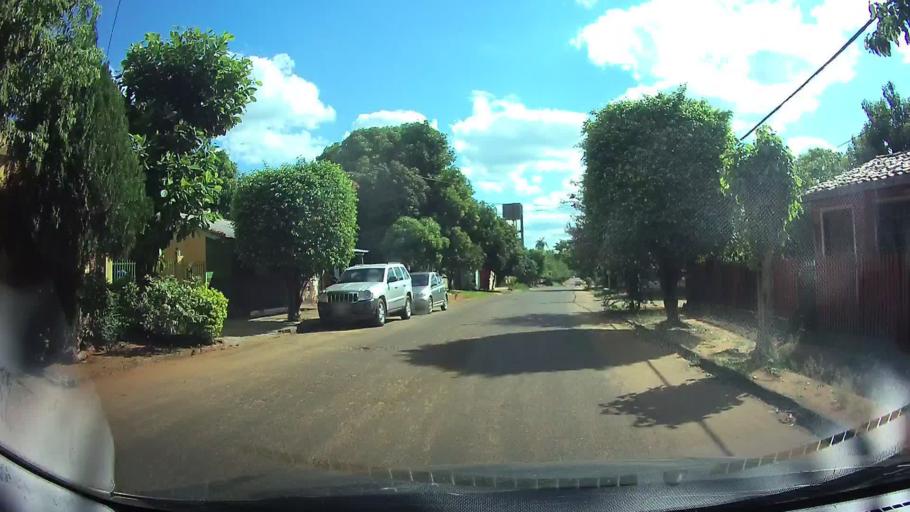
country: PY
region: Central
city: Itaugua
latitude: -25.3873
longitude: -57.3473
